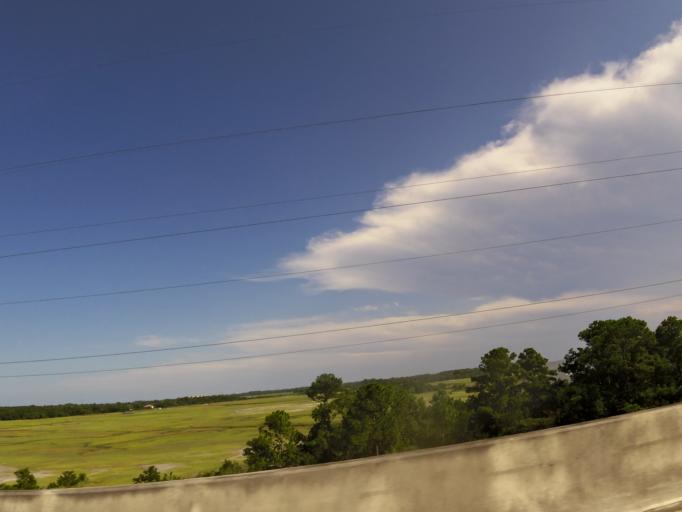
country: US
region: Florida
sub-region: Nassau County
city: Fernandina Beach
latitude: 30.6286
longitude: -81.4818
